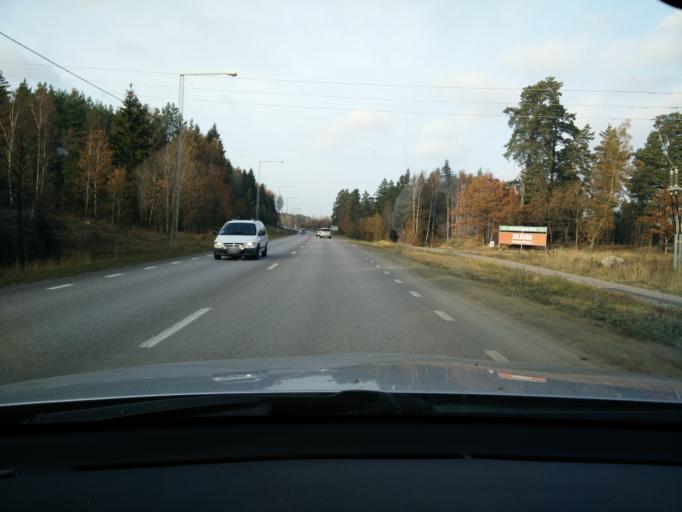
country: SE
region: Stockholm
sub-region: Taby Kommun
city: Taby
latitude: 59.4776
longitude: 18.1207
